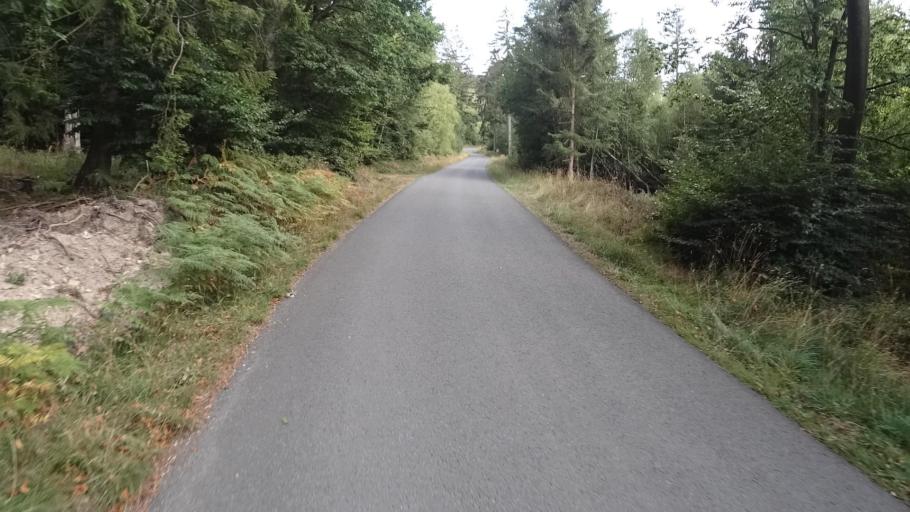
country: DE
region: Rheinland-Pfalz
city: Dichtelbach
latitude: 49.9923
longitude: 7.7061
